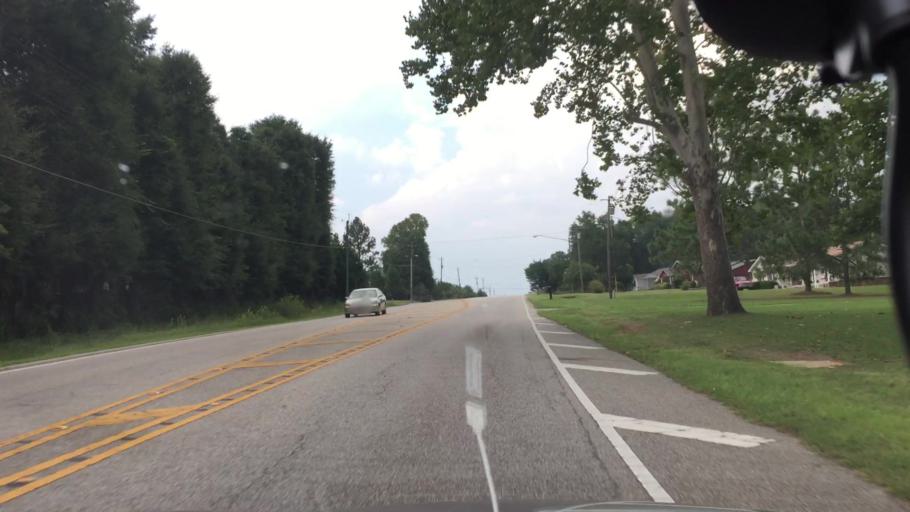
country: US
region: Alabama
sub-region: Coffee County
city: Enterprise
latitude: 31.3616
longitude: -85.8313
